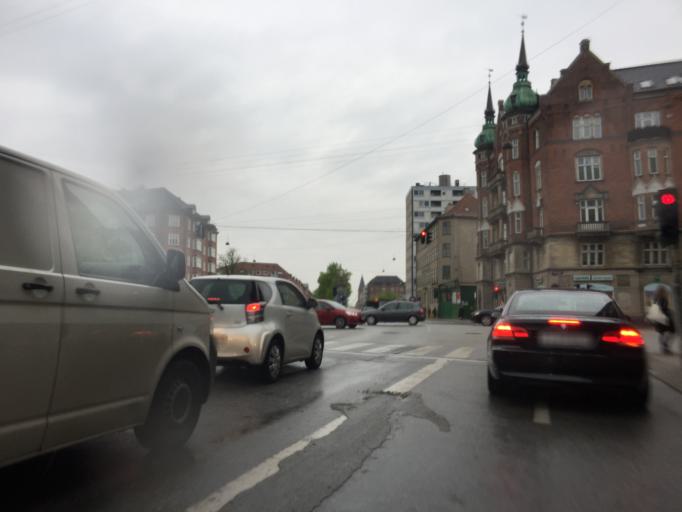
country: DK
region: Capital Region
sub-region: Kobenhavn
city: Copenhagen
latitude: 55.7093
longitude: 12.5781
